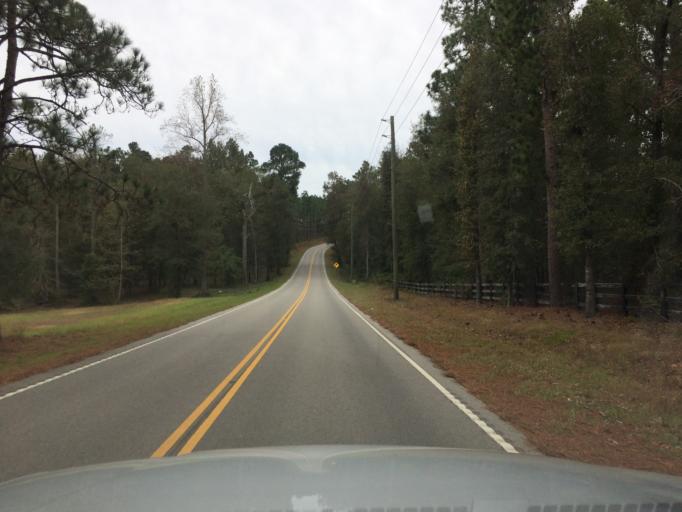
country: US
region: South Carolina
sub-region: Aiken County
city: New Ellenton
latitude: 33.4751
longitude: -81.6571
